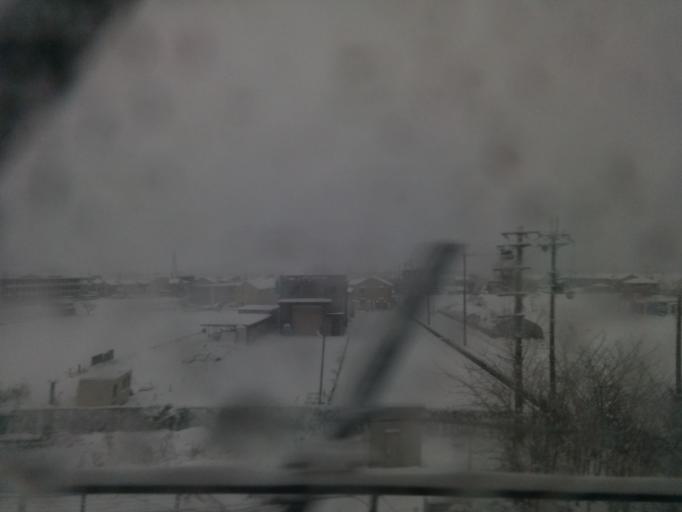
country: JP
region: Shiga Prefecture
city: Hikone
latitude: 35.2374
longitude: 136.2657
